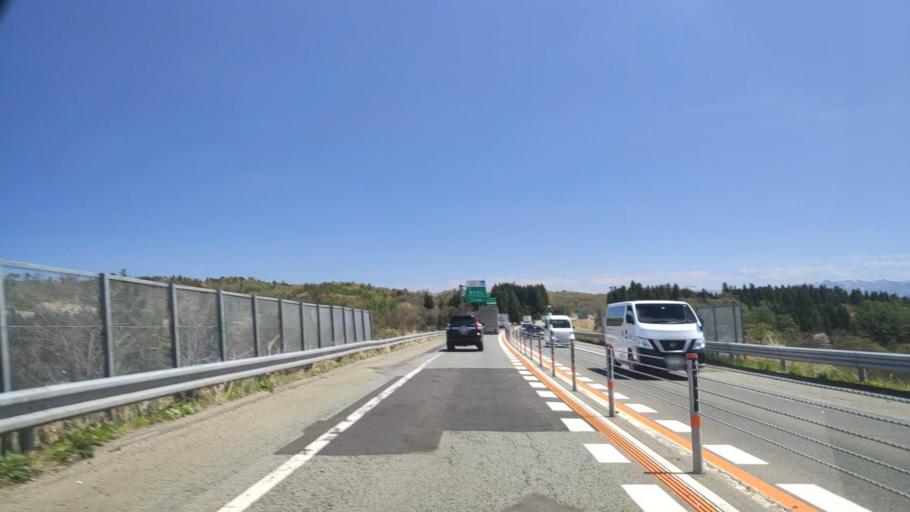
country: JP
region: Yamagata
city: Obanazawa
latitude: 38.6646
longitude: 140.3552
